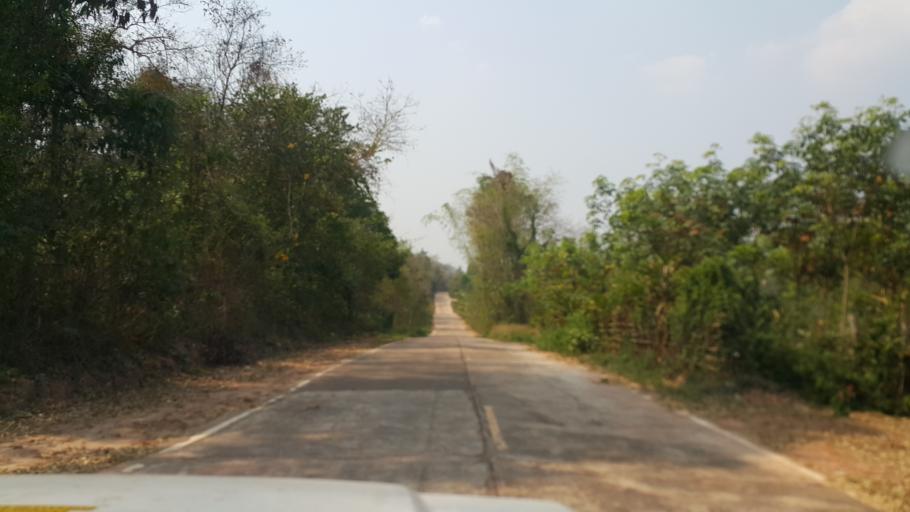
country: TH
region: Nakhon Phanom
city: Ban Phaeng
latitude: 17.9584
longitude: 104.1573
